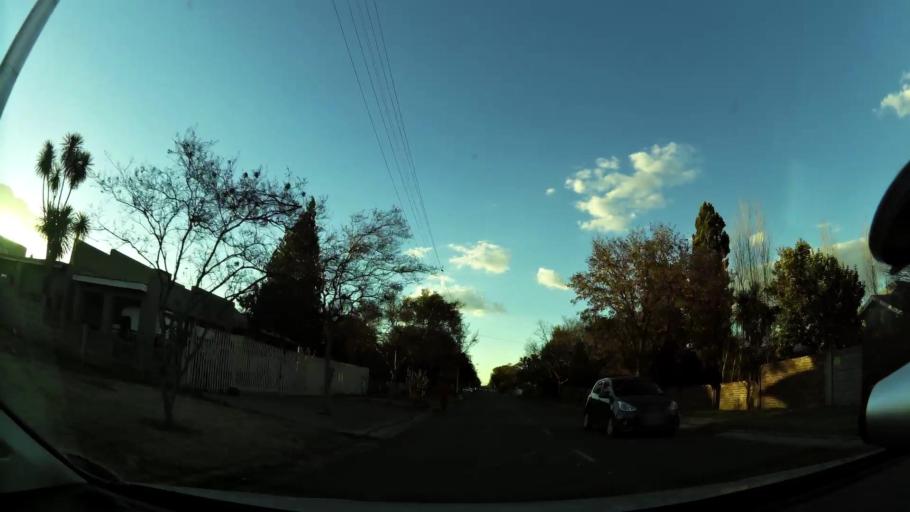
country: ZA
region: North-West
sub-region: Dr Kenneth Kaunda District Municipality
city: Potchefstroom
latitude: -26.7197
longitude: 27.0926
